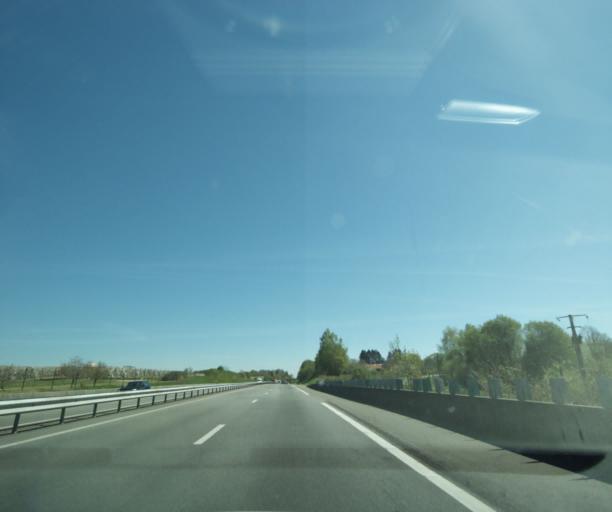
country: FR
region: Limousin
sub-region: Departement de la Haute-Vienne
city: Vicq-sur-Breuilh
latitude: 45.6443
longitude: 1.4119
